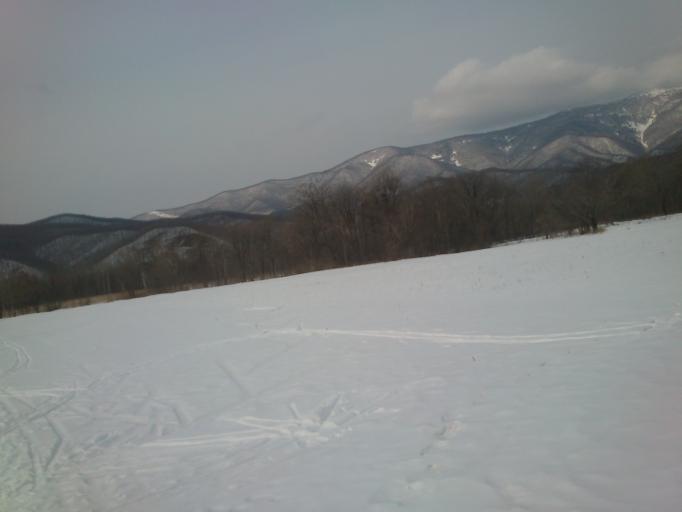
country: RU
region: Primorskiy
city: Volchanets
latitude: 43.1728
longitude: 132.7406
